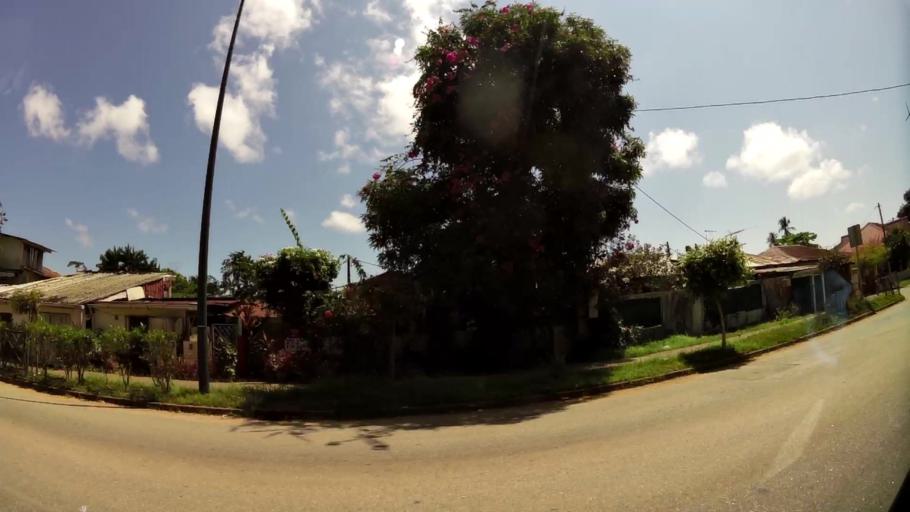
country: GF
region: Guyane
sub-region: Guyane
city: Cayenne
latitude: 4.9204
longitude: -52.3206
